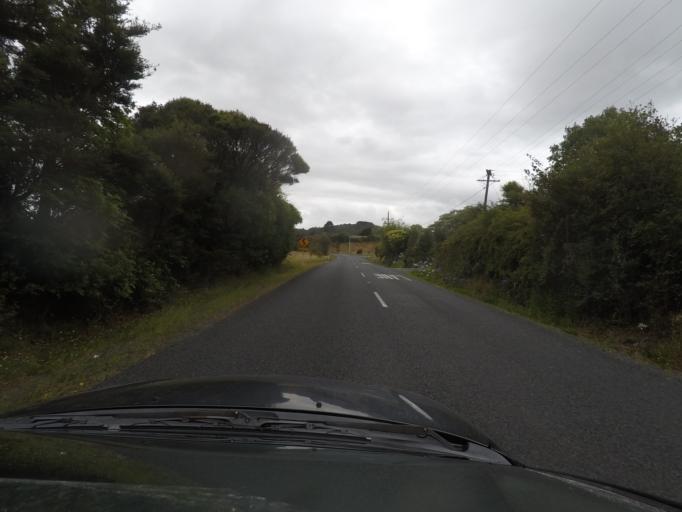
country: NZ
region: Auckland
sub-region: Auckland
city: Wellsford
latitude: -36.2809
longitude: 174.5787
